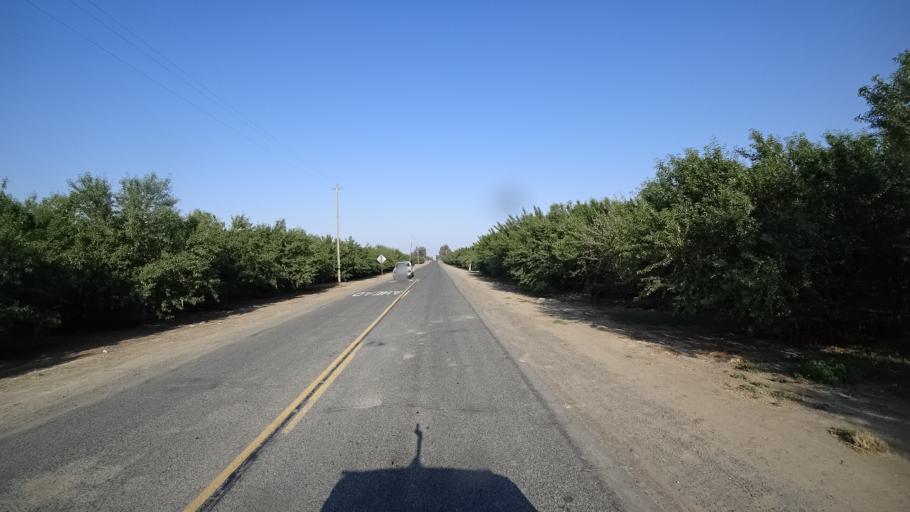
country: US
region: California
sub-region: Fresno County
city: Riverdale
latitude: 36.3804
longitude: -119.8113
